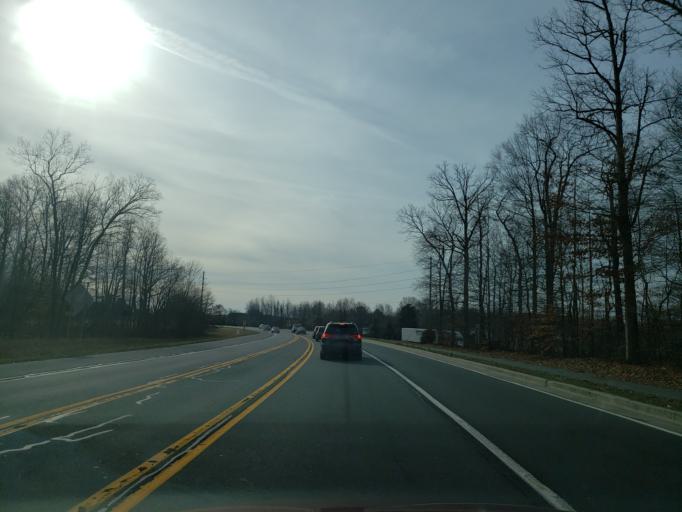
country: US
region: Delaware
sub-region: Kent County
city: Cheswold
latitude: 39.1835
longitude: -75.5606
